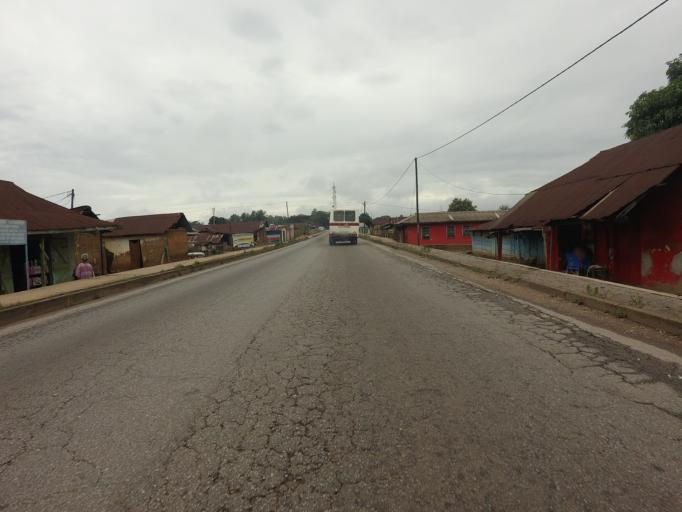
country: GH
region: Eastern
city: Begoro
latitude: 6.4330
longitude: -0.5842
